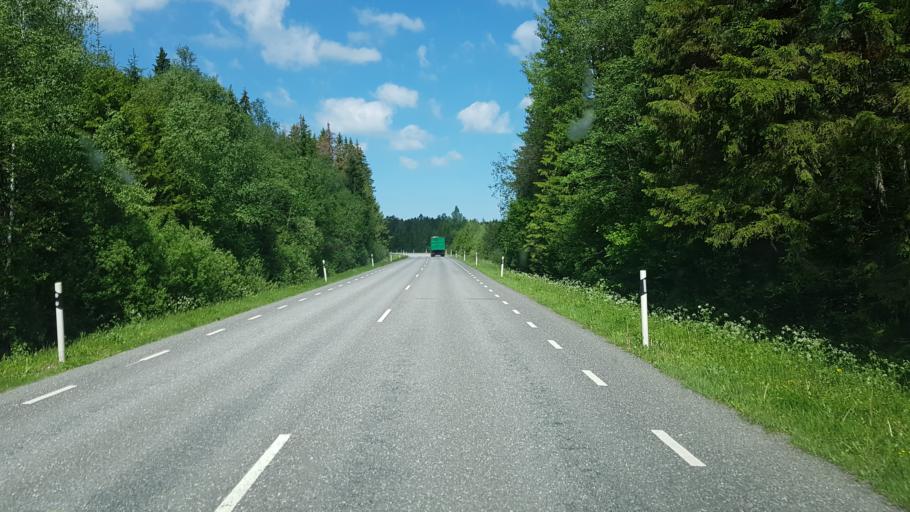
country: EE
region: Laeaene-Virumaa
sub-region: Rakke vald
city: Rakke
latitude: 59.0464
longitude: 26.2389
